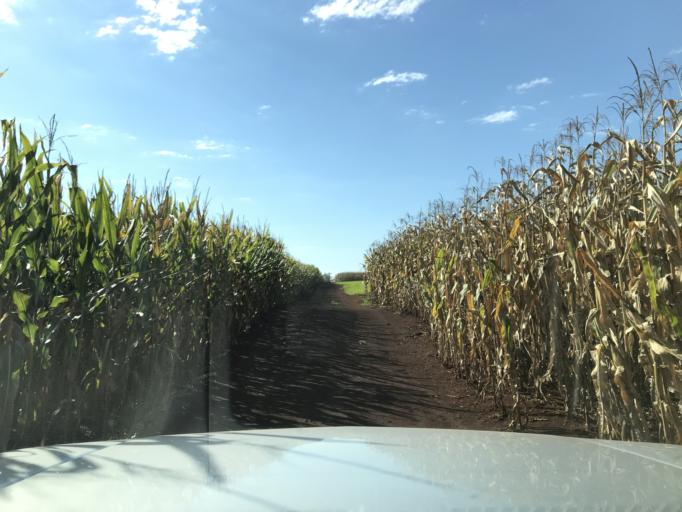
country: BR
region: Parana
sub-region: Palotina
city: Palotina
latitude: -24.2639
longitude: -53.8112
